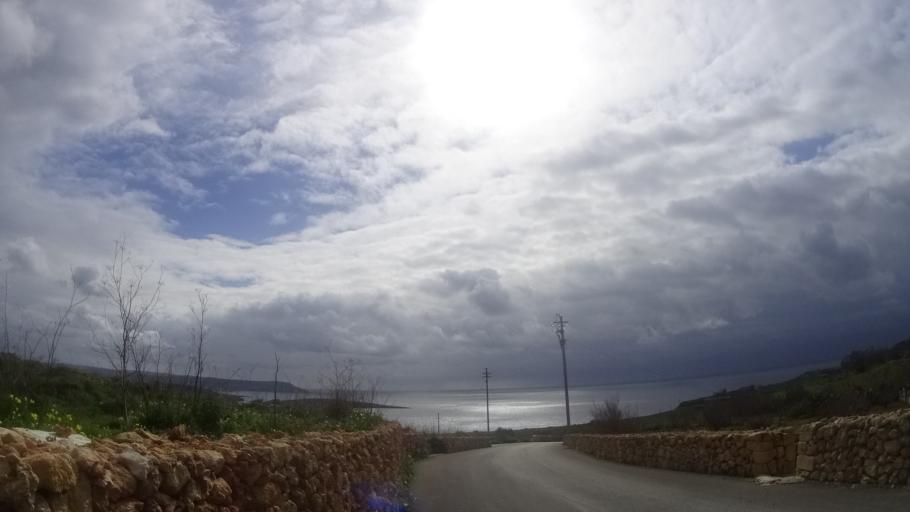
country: MT
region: Il-Qala
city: Qala
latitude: 36.0315
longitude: 14.3215
